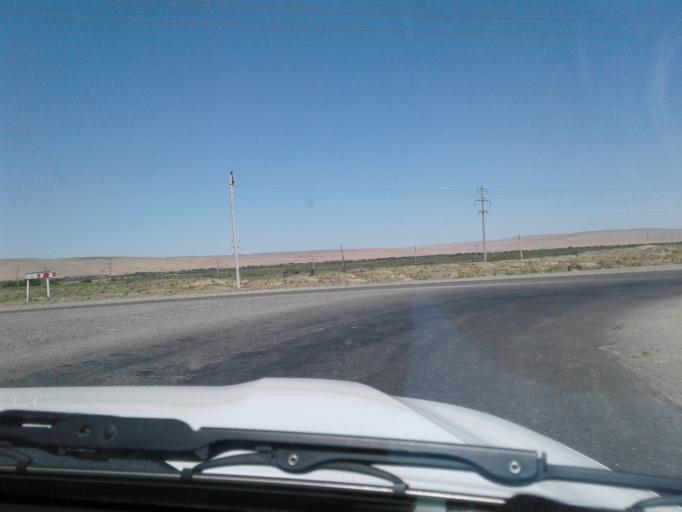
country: AF
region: Badghis
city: Bala Murghab
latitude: 35.9697
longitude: 62.8014
